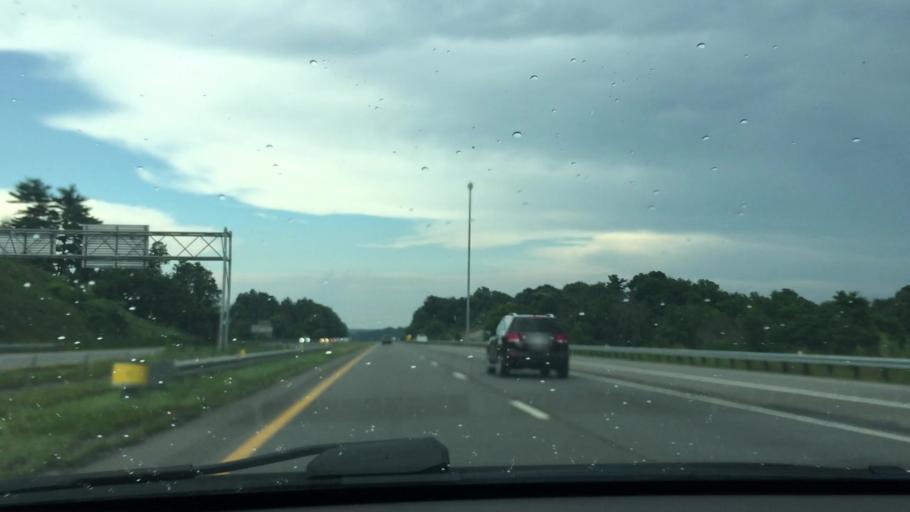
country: US
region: Ohio
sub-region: Belmont County
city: Wolfhurst
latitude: 40.0490
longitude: -80.7912
